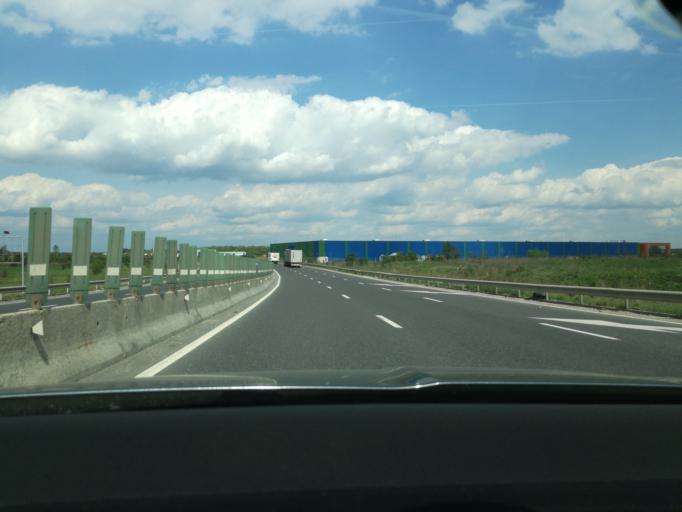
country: RO
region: Ilfov
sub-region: Comuna Chitila
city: Chitila
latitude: 44.5010
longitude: 26.0014
